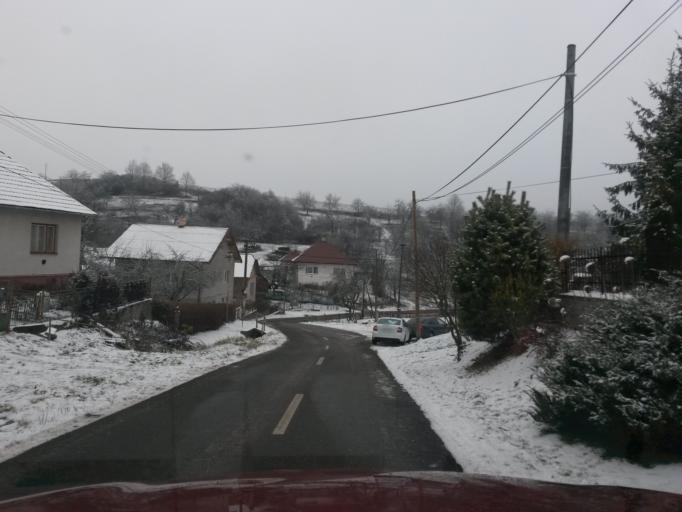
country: SK
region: Presovsky
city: Sabinov
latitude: 48.9885
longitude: 21.0786
